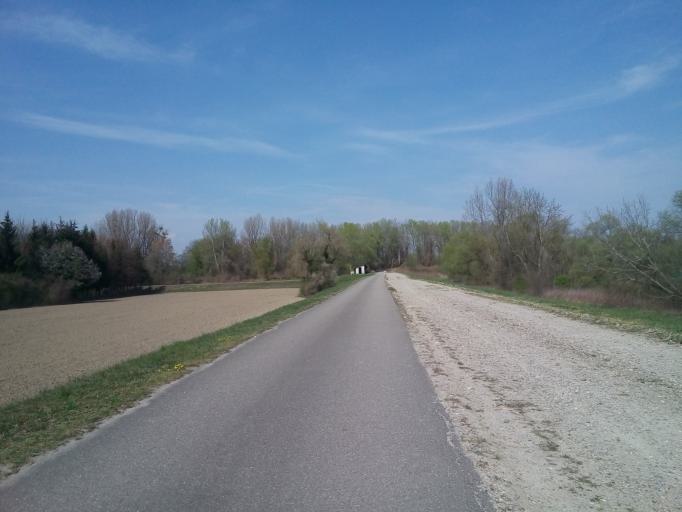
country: FR
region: Alsace
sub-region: Departement du Bas-Rhin
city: Seltz
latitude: 48.8666
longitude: 8.1094
